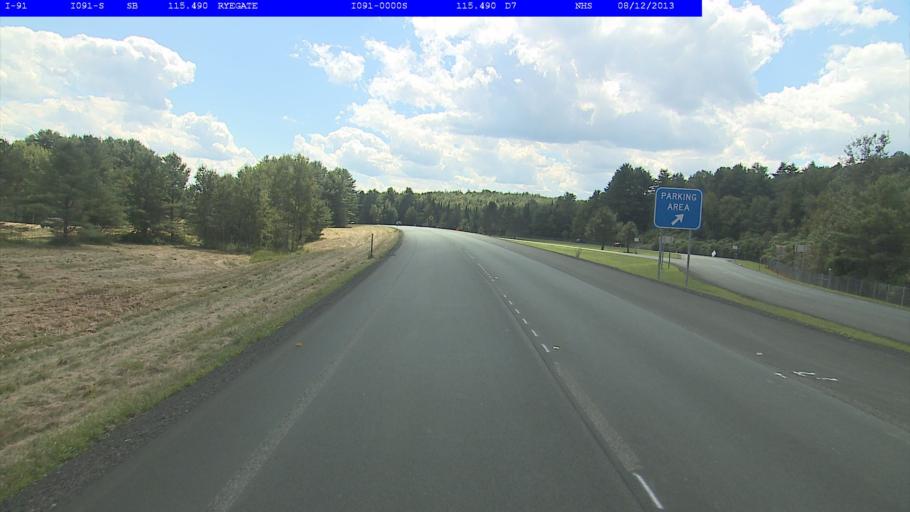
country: US
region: New Hampshire
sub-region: Grafton County
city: Woodsville
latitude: 44.2322
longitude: -72.0696
